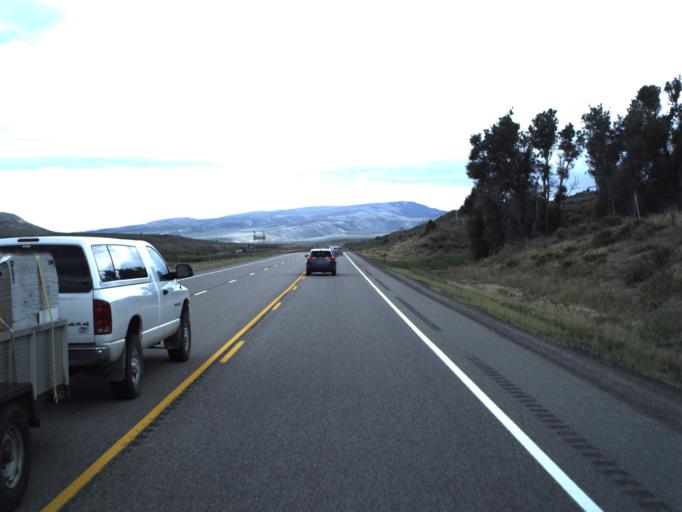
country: US
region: Utah
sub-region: Carbon County
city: Helper
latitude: 39.9050
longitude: -111.0591
